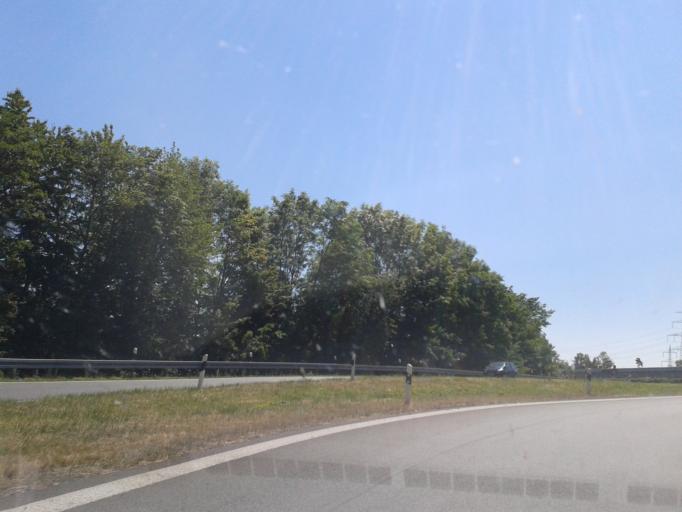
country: DE
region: North Rhine-Westphalia
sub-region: Regierungsbezirk Detmold
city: Paderborn
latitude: 51.7322
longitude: 8.7070
